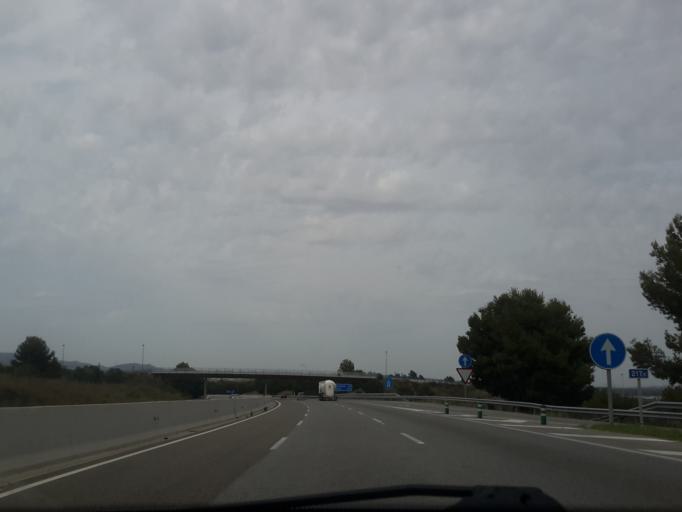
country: ES
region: Catalonia
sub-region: Provincia de Tarragona
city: El Vendrell
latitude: 41.2261
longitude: 1.5242
